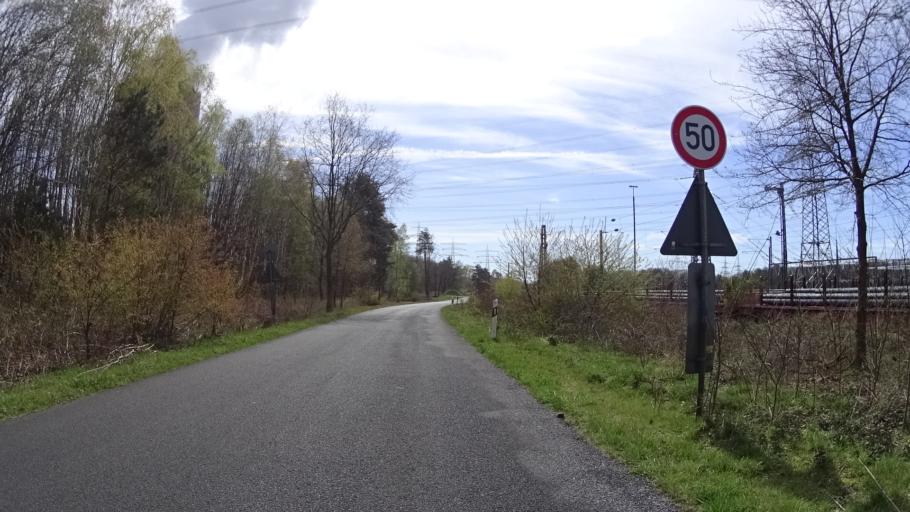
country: DE
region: Lower Saxony
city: Lingen
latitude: 52.4759
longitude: 7.3130
